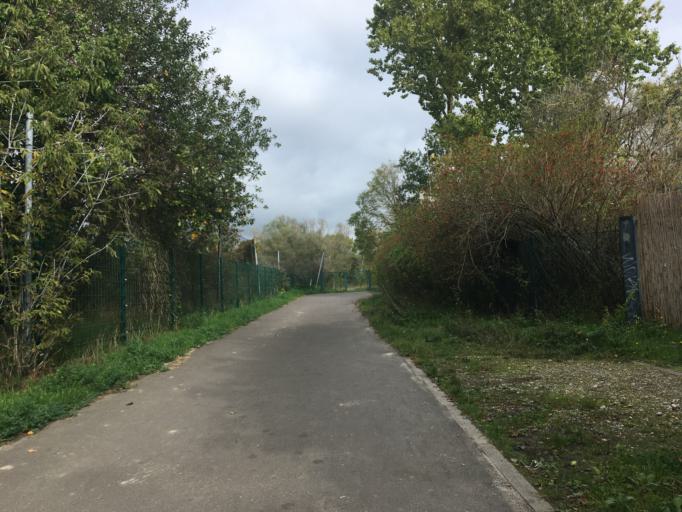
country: DE
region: Berlin
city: Kladow
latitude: 52.4627
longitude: 13.1481
